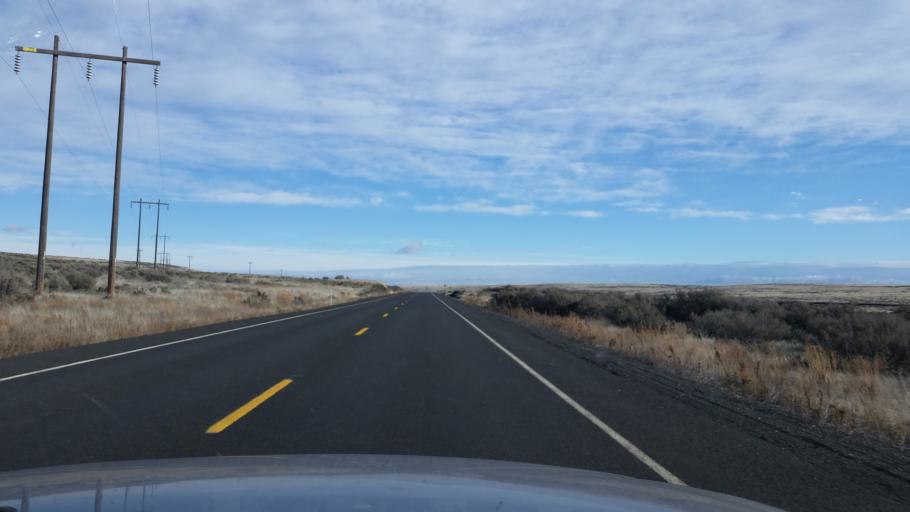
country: US
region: Washington
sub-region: Adams County
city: Ritzville
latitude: 47.3477
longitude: -118.5912
